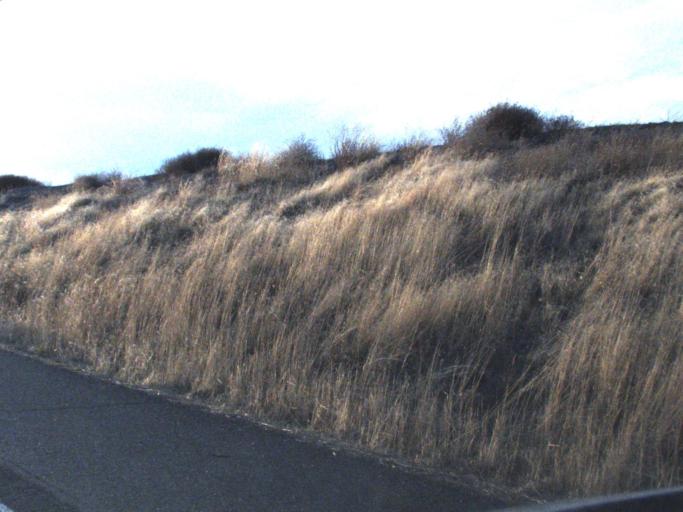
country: US
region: Washington
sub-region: Benton County
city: Finley
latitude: 46.0647
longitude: -118.8414
